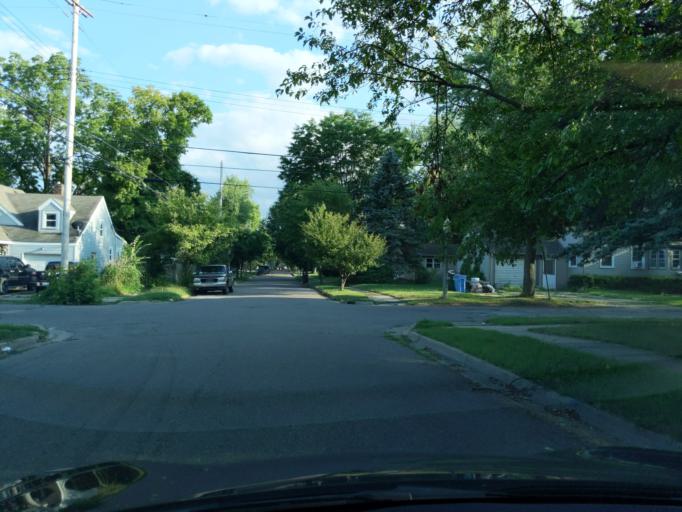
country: US
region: Michigan
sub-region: Ingham County
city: Lansing
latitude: 42.6879
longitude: -84.5505
